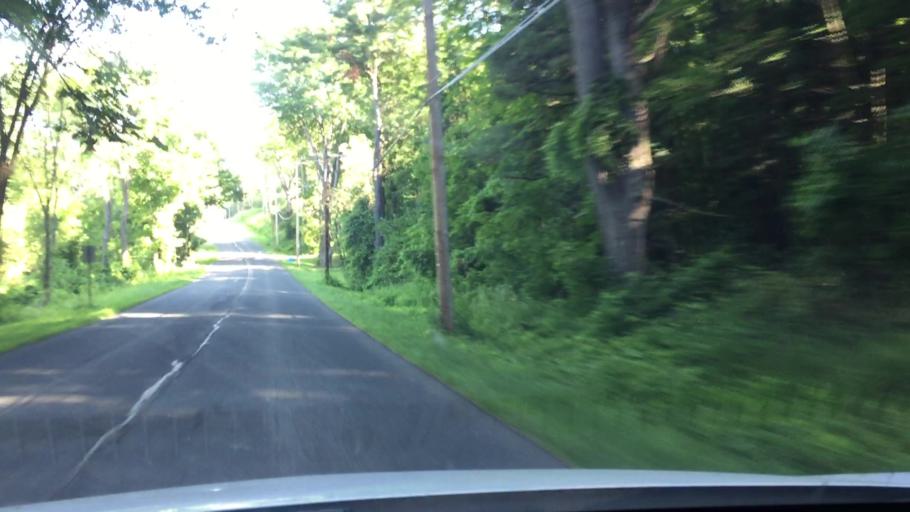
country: US
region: Massachusetts
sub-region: Berkshire County
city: Lee
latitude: 42.2657
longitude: -73.2307
